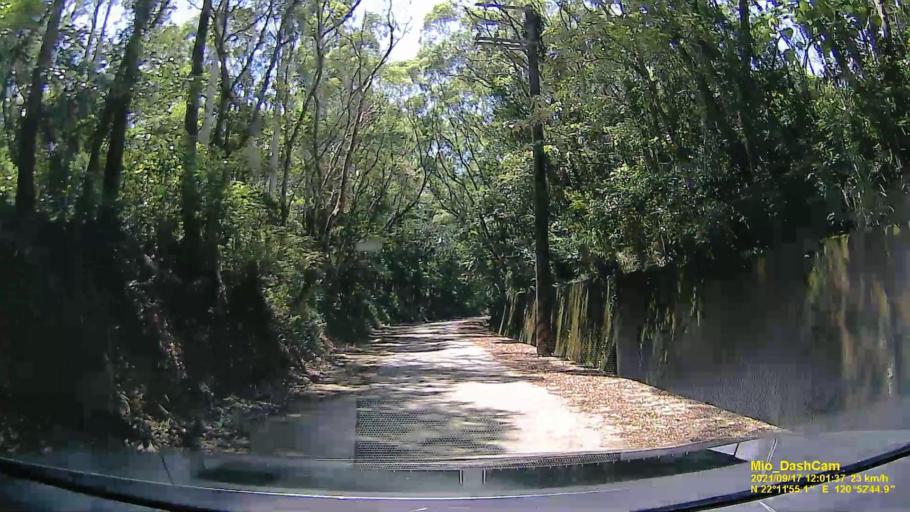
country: TW
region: Taiwan
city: Hengchun
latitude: 22.1986
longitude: 120.8791
